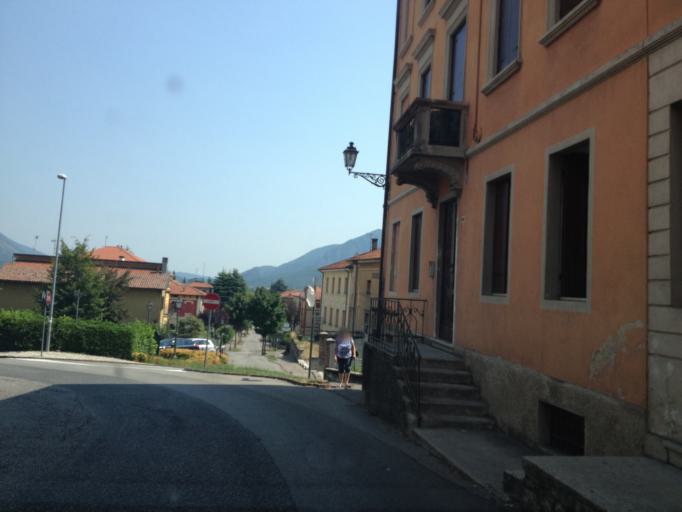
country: IT
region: Veneto
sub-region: Provincia di Vicenza
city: Arsiero
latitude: 45.8032
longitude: 11.3511
